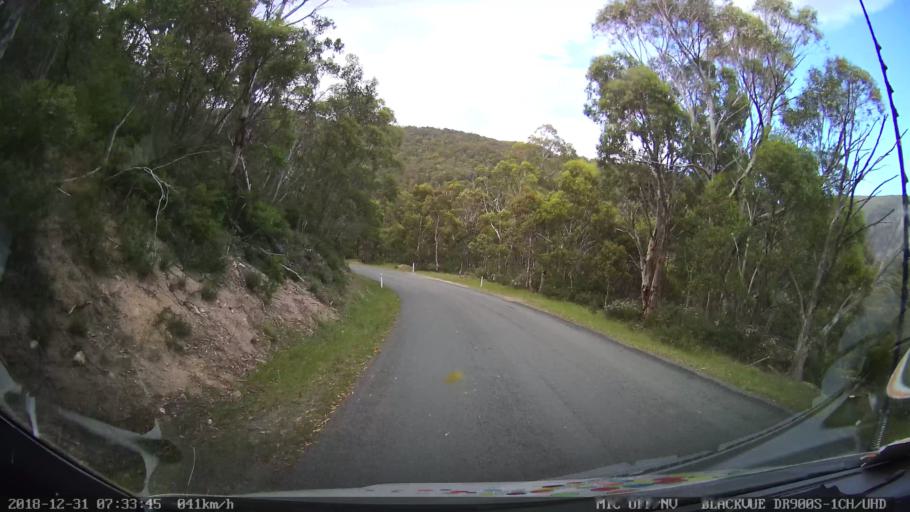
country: AU
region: New South Wales
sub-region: Snowy River
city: Jindabyne
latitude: -36.3335
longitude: 148.4548
